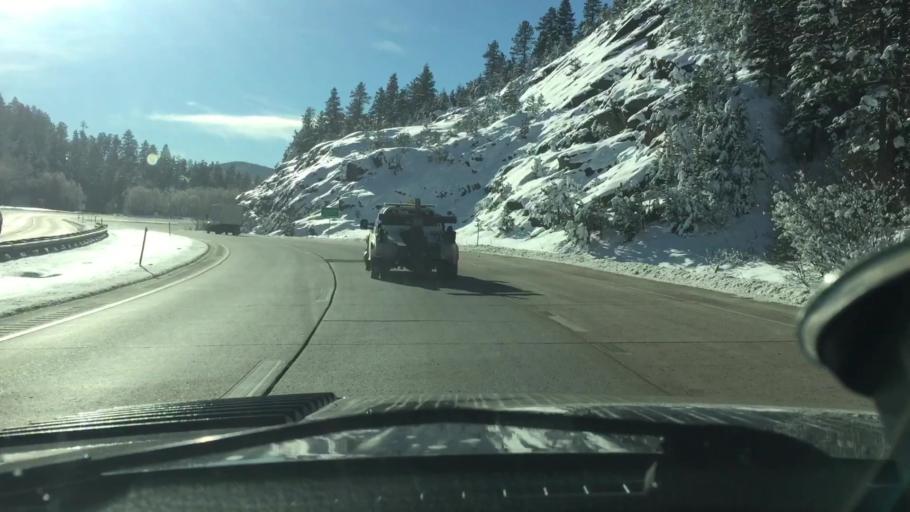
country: US
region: Colorado
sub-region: Jefferson County
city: Indian Hills
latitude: 39.6142
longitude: -105.2330
